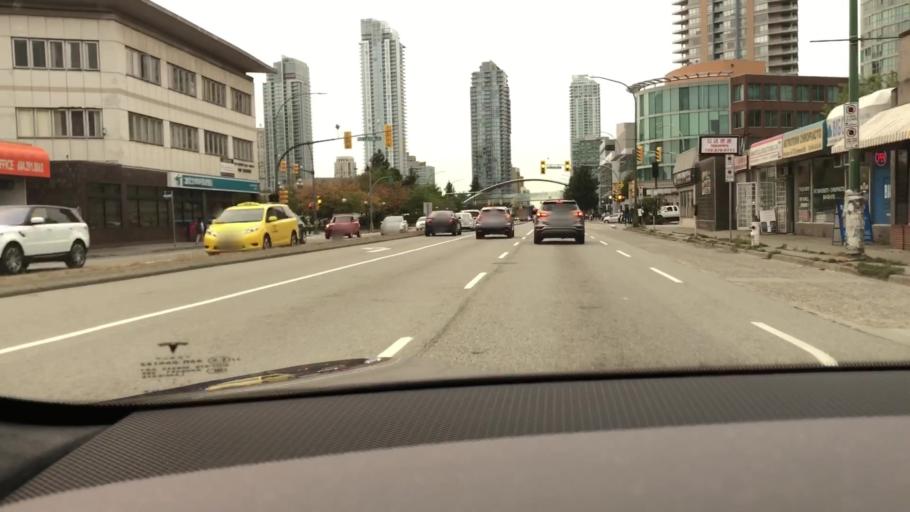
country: CA
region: British Columbia
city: Burnaby
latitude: 49.2264
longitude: -122.9933
